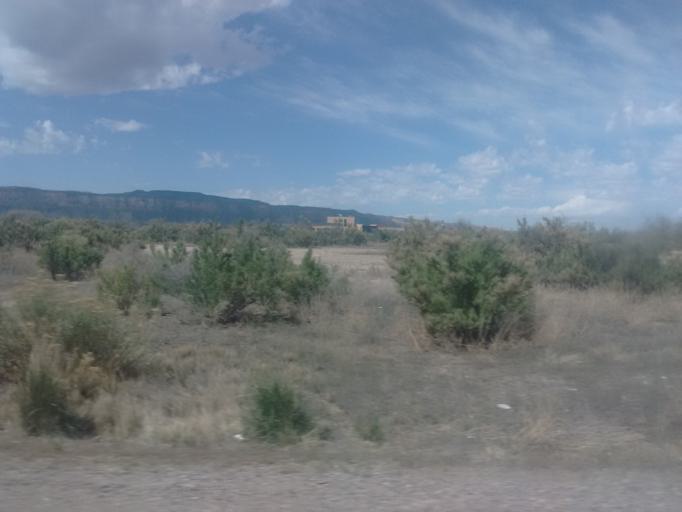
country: US
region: Colorado
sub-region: Mesa County
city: Redlands
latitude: 39.1054
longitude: -108.6082
